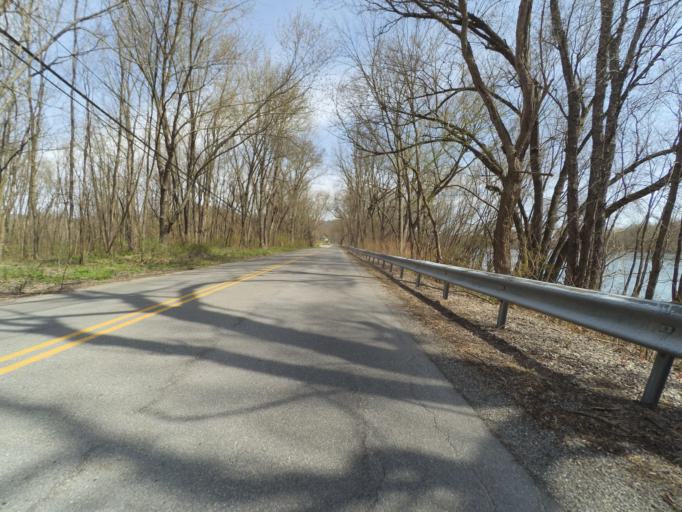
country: US
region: Pennsylvania
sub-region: Clinton County
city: Avis
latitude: 41.1670
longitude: -77.3664
